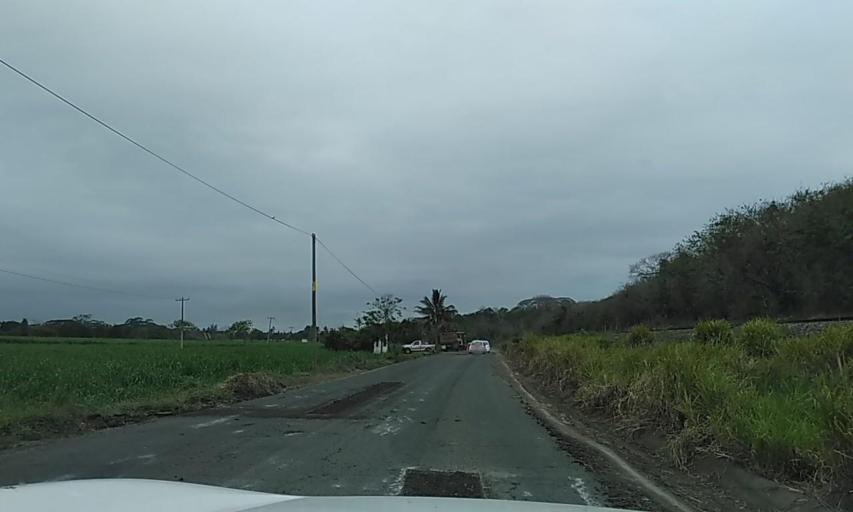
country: MX
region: Veracruz
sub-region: La Antigua
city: Nicolas Blanco (San Pancho)
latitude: 19.3087
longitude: -96.3178
